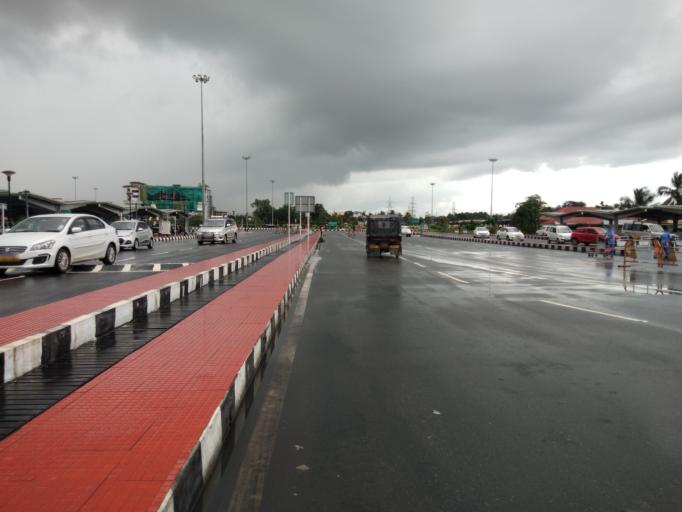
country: IN
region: Kerala
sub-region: Ernakulam
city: Angamali
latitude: 10.1562
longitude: 76.3911
